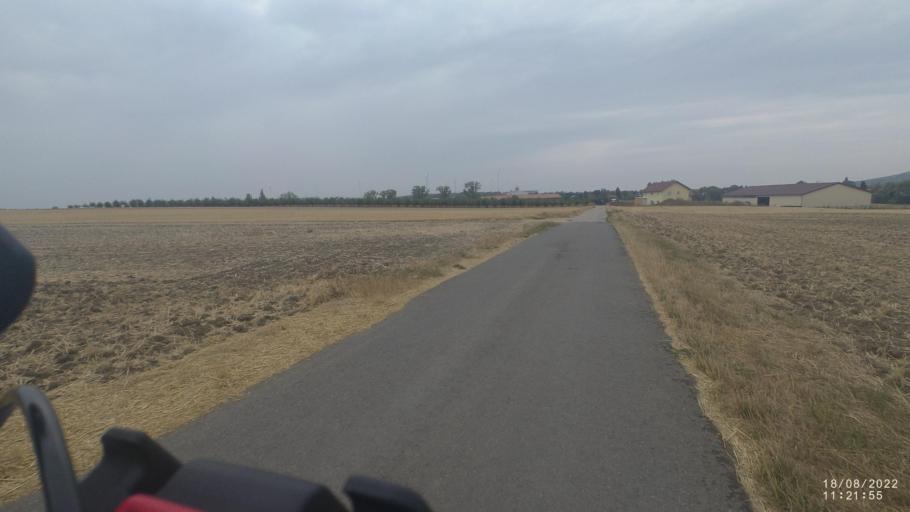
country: DE
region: Rheinland-Pfalz
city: Wallertheim
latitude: 49.8327
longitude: 8.0621
